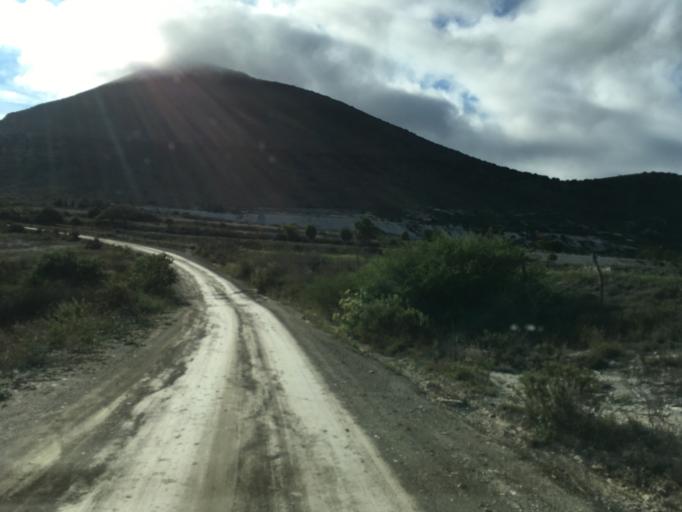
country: MX
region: Hidalgo
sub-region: Cardonal
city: Pozuelos
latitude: 20.6248
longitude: -98.9798
